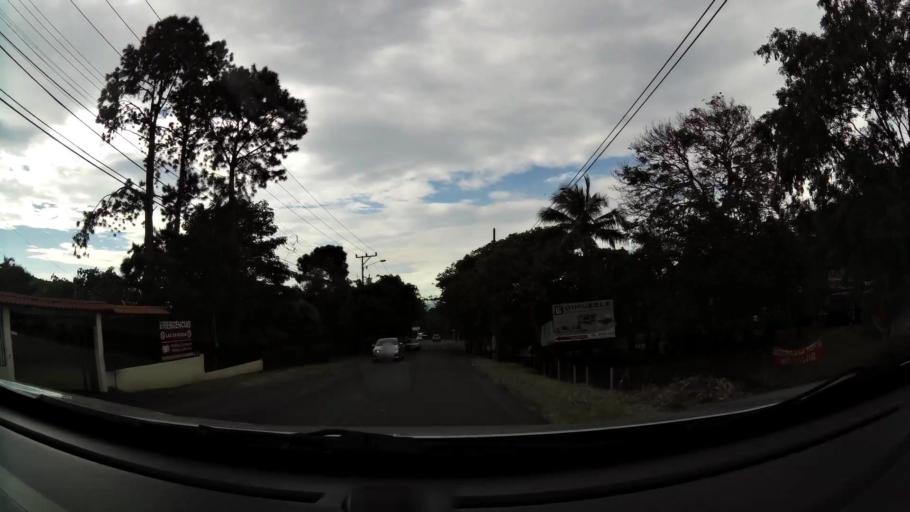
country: CR
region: San Jose
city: Santa Ana
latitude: 9.9297
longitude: -84.1743
